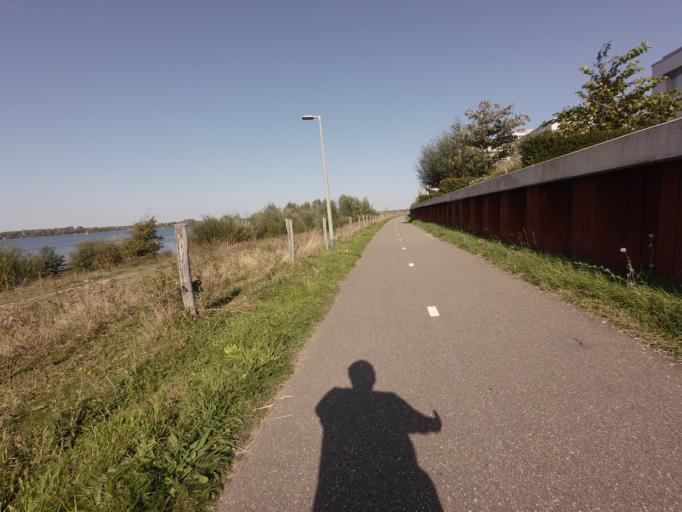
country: NL
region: Limburg
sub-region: Gemeente Roermond
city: Roermond
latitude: 51.1758
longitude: 5.9529
